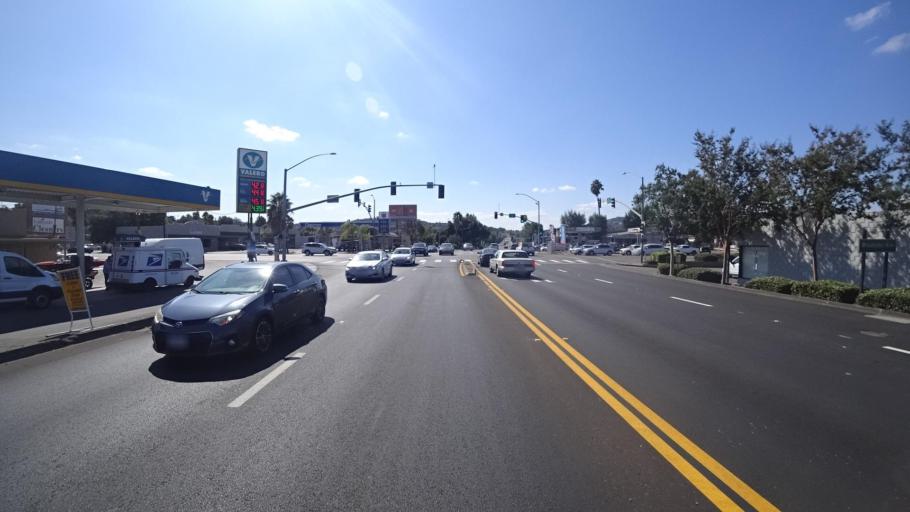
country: US
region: California
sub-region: San Diego County
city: Lakeside
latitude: 32.8565
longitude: -116.9312
